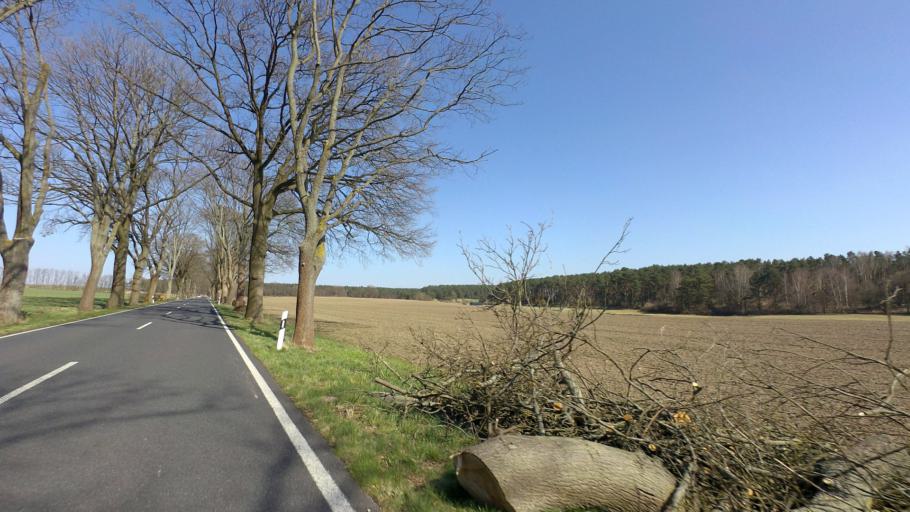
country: DE
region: Brandenburg
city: Sonnenberg
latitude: 52.9914
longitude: 13.0577
